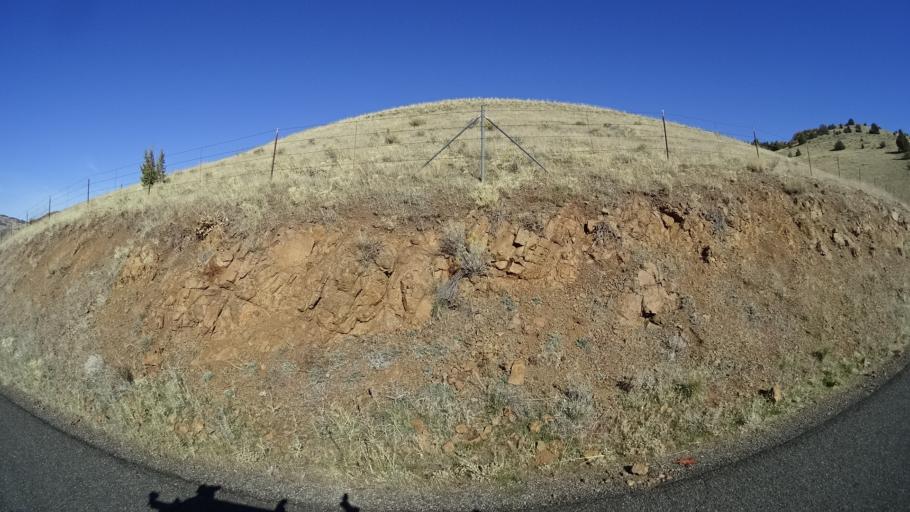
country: US
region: California
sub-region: Siskiyou County
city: Montague
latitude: 41.8247
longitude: -122.3439
